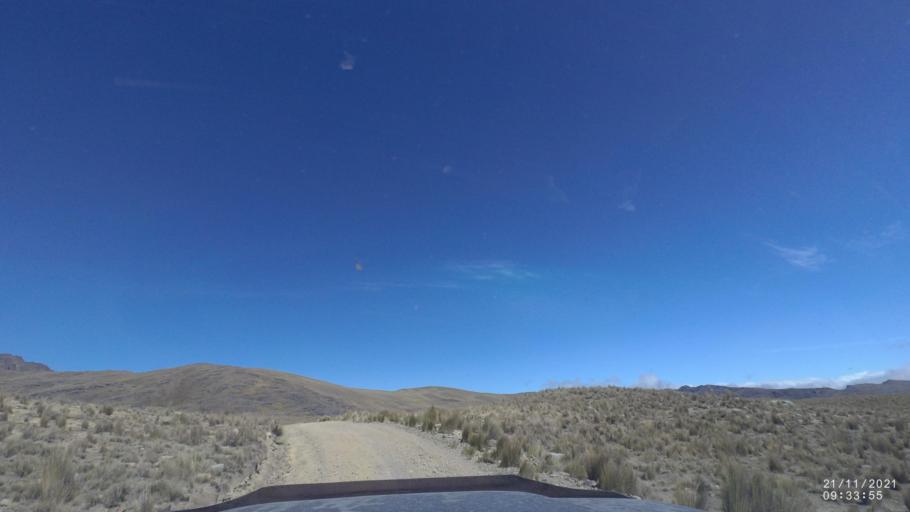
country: BO
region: Cochabamba
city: Cochabamba
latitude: -17.0583
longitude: -66.2582
